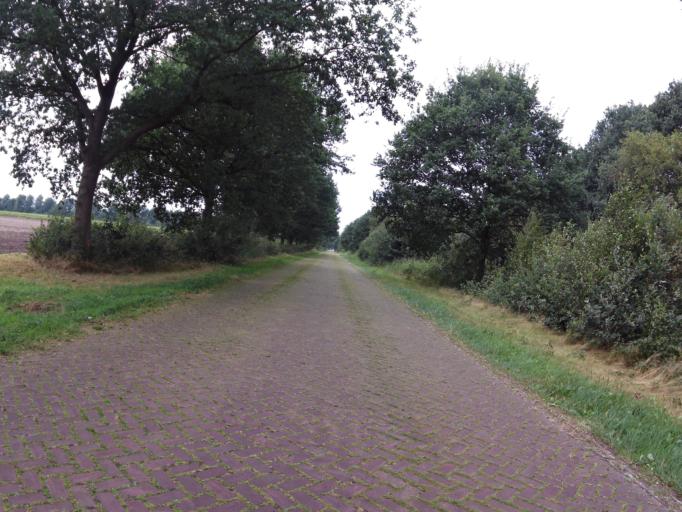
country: NL
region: Drenthe
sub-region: Gemeente Emmen
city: Klazienaveen
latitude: 52.6752
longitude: 6.9578
